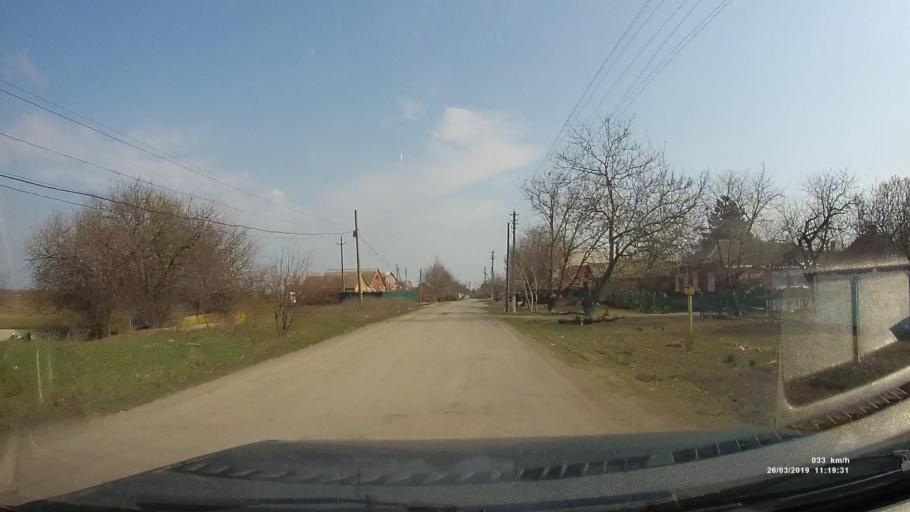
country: RU
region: Krasnodarskiy
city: Shabel'skoye
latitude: 47.1352
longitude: 38.5399
